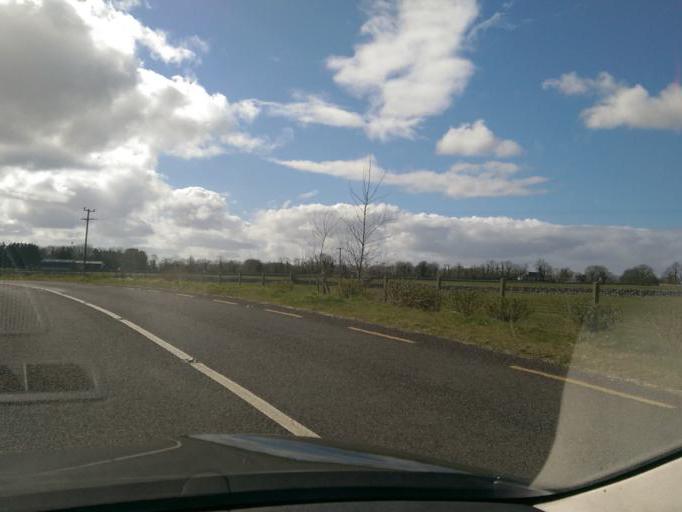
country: IE
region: Connaught
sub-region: County Galway
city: Athenry
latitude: 53.3511
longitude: -8.7490
